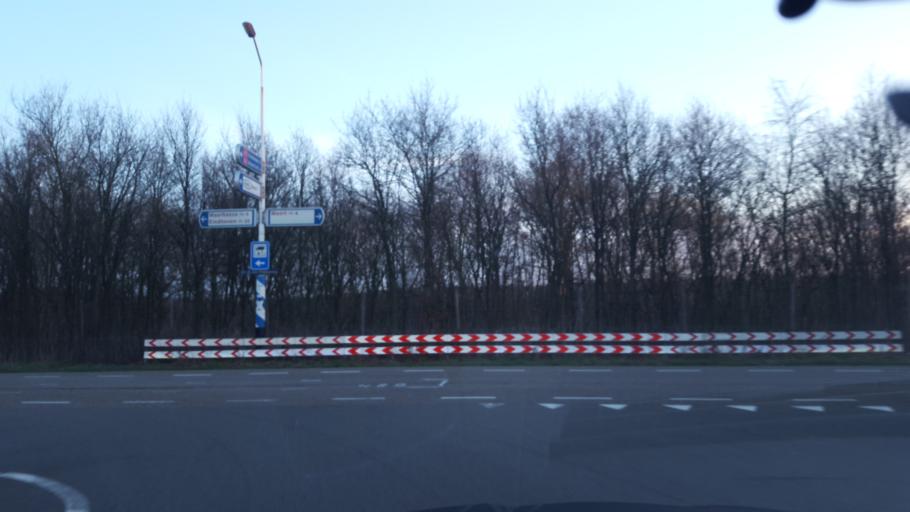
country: NL
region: Limburg
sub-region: Gemeente Weert
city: Weert
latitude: 51.2779
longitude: 5.6641
